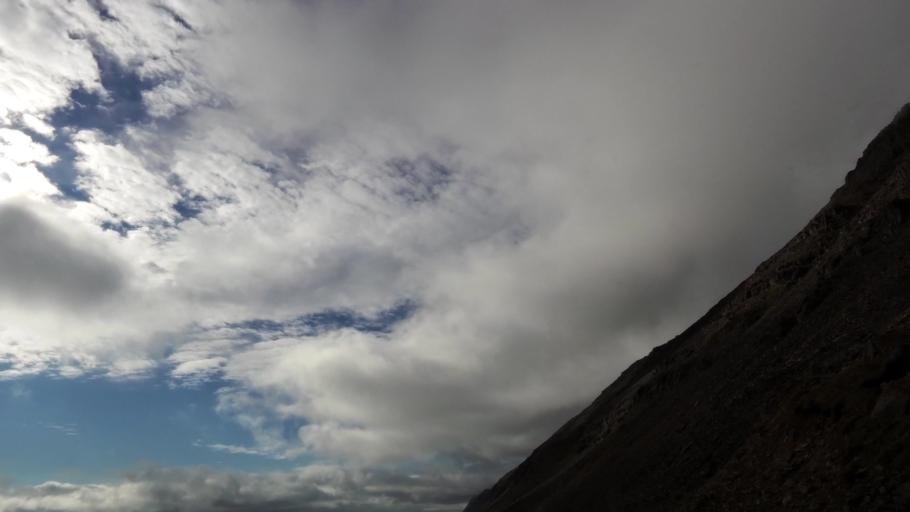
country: IS
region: West
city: Olafsvik
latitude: 65.5582
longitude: -23.9039
